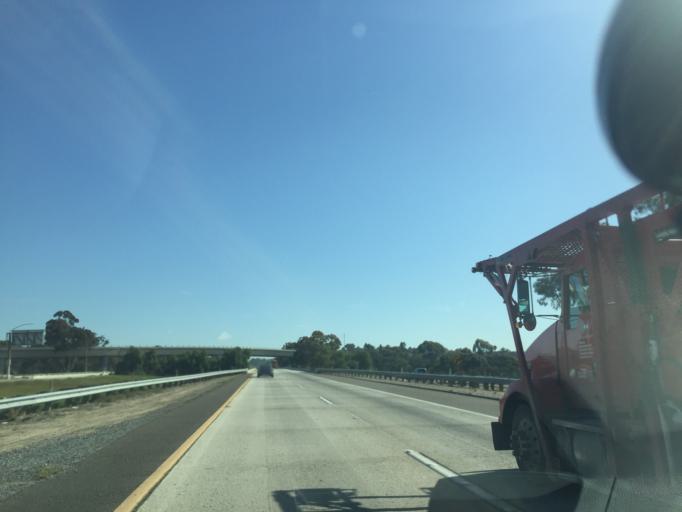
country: US
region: California
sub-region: San Diego County
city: Imperial Beach
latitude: 32.5681
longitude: -117.0423
